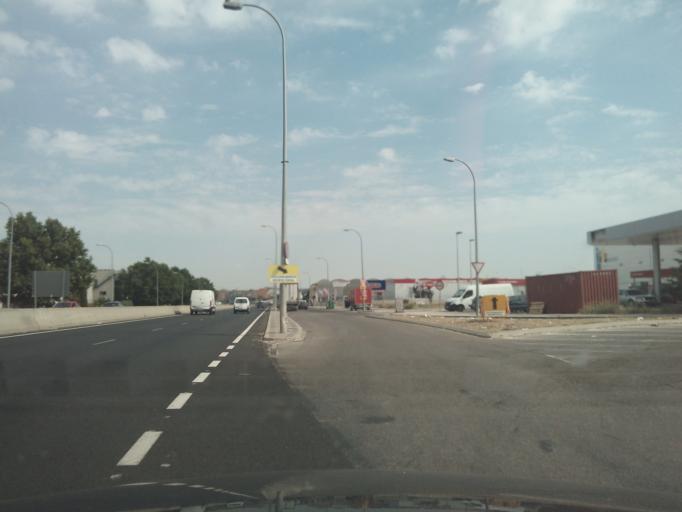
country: ES
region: Madrid
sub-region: Provincia de Madrid
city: Torrejon de Ardoz
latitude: 40.4469
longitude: -3.4816
